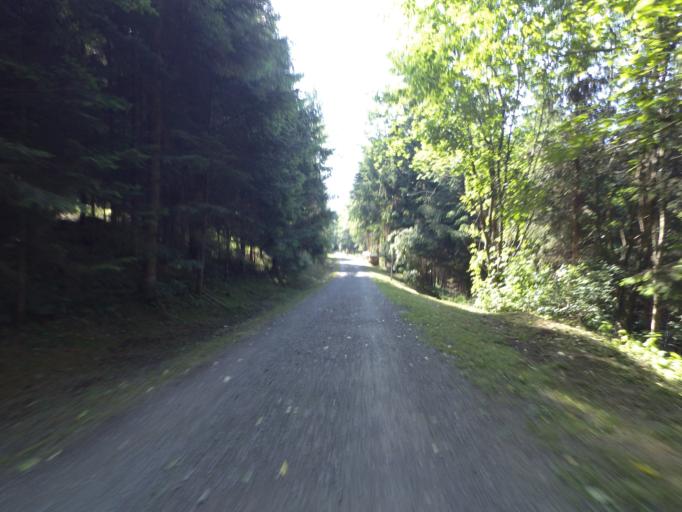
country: AT
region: Carinthia
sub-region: Politischer Bezirk Spittal an der Drau
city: Millstatt
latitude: 46.8019
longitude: 13.5463
